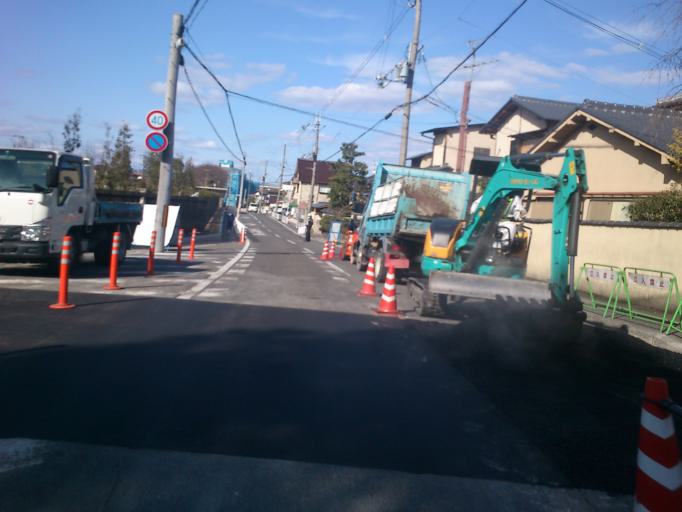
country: JP
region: Kyoto
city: Muko
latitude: 34.9243
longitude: 135.6855
